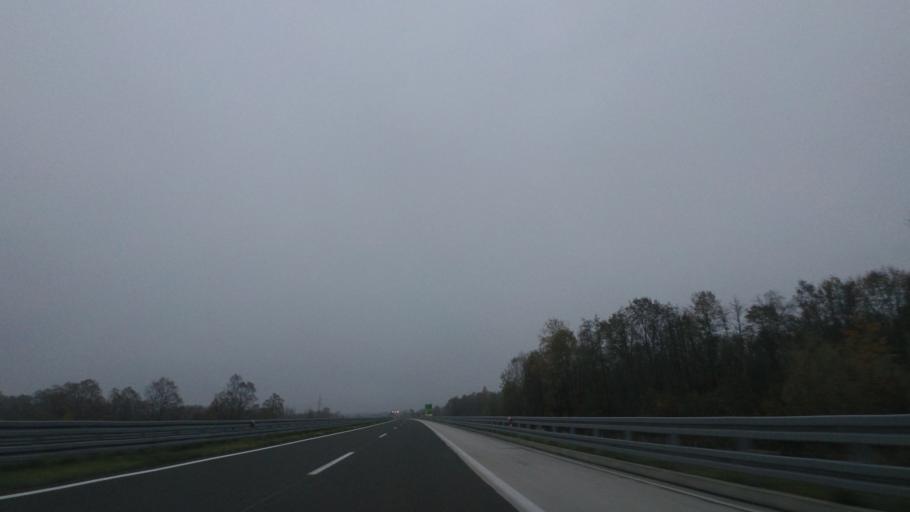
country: HR
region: Sisacko-Moslavacka
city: Lekenik
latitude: 45.5734
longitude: 16.2052
